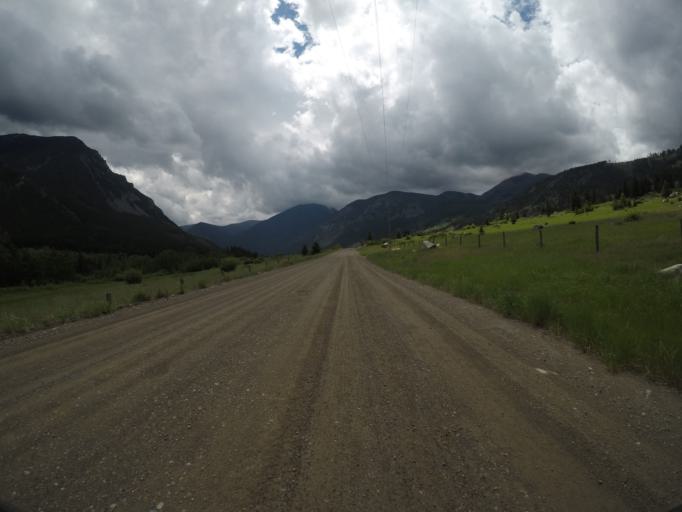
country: US
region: Montana
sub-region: Park County
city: Livingston
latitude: 45.5303
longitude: -110.2159
